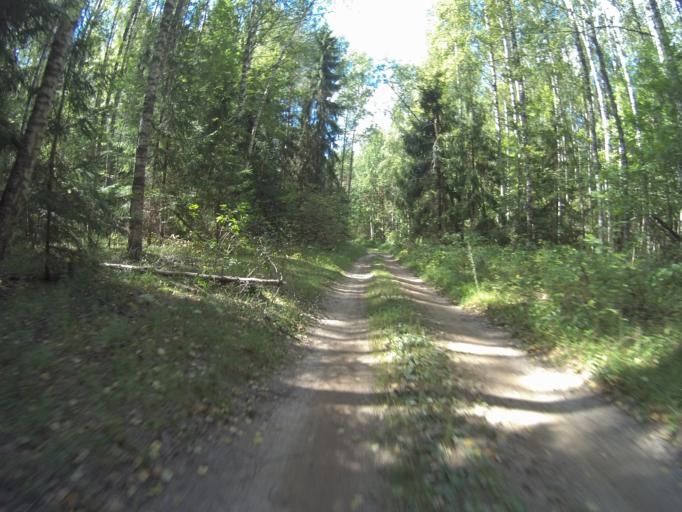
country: RU
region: Vladimir
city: Sobinka
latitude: 55.8871
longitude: 40.1631
